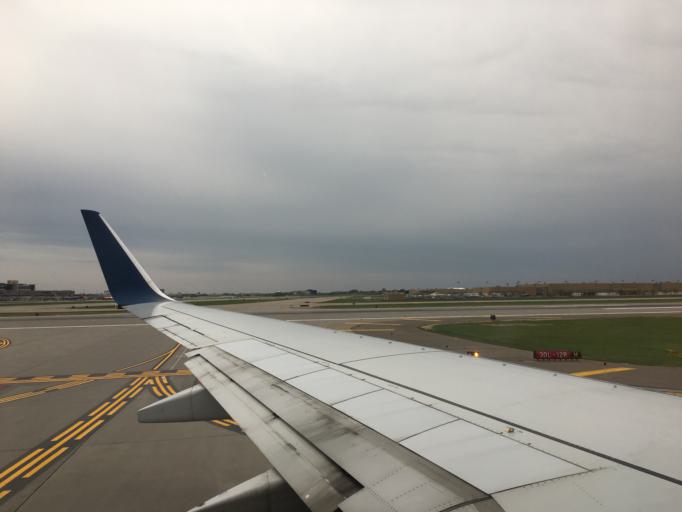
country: US
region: Minnesota
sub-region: Hennepin County
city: Richfield
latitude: 44.8847
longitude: -93.2238
